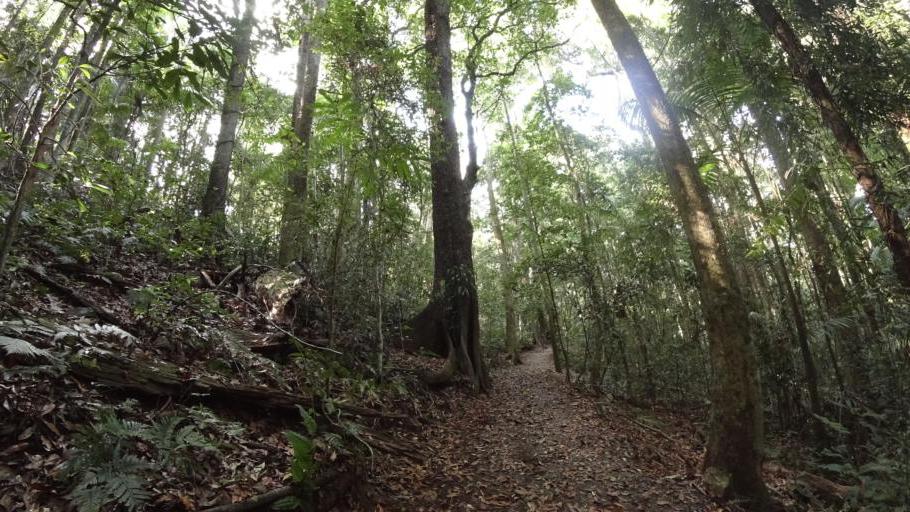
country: AU
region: Queensland
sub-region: Moreton Bay
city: Highvale
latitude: -27.4008
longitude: 152.7915
